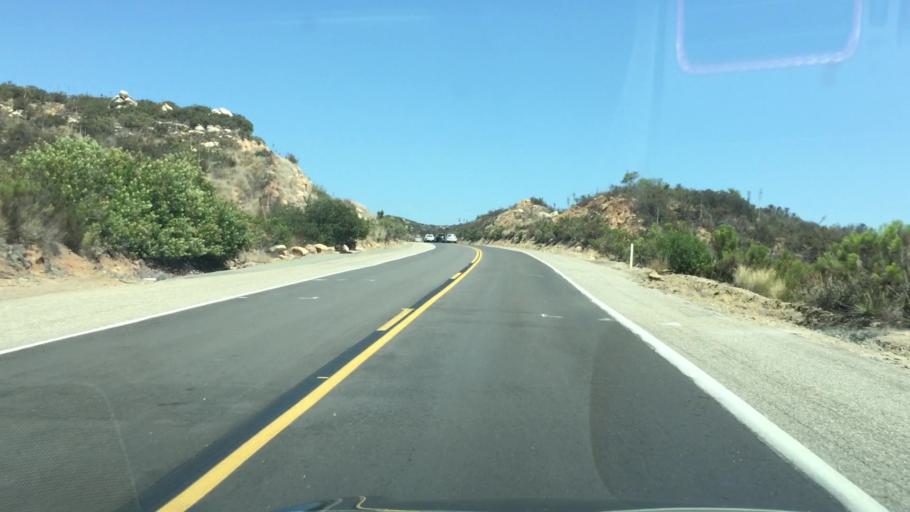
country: US
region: California
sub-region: San Diego County
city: Jamul
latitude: 32.7345
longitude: -116.8385
